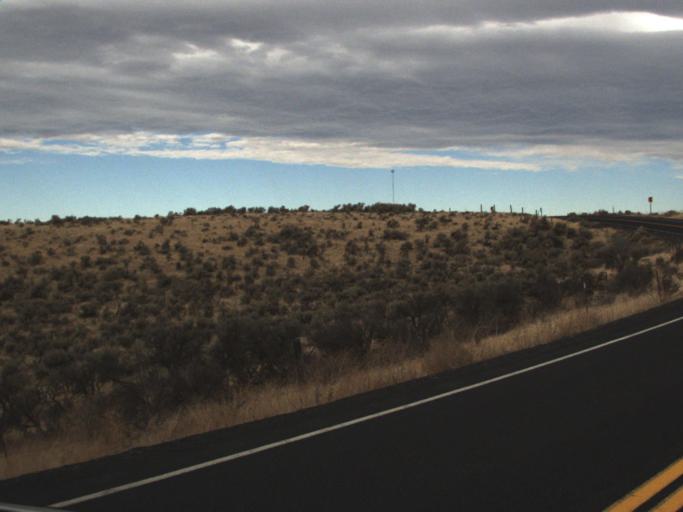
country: US
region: Washington
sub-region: Adams County
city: Ritzville
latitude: 47.4717
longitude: -118.7737
